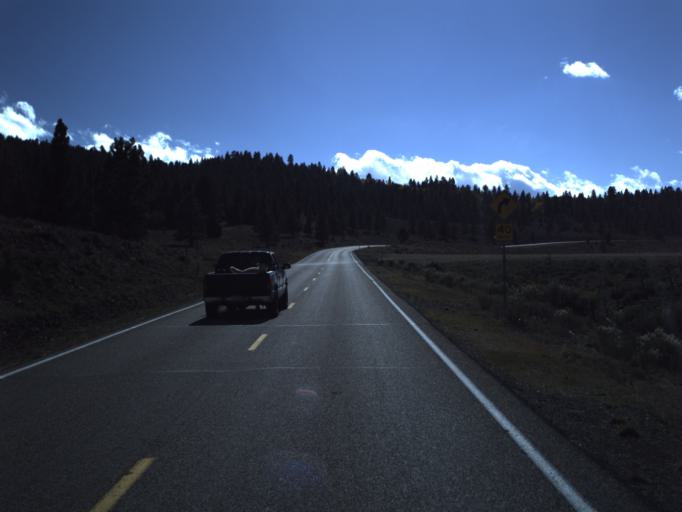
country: US
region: Utah
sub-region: Garfield County
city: Panguitch
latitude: 37.7253
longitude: -112.6123
